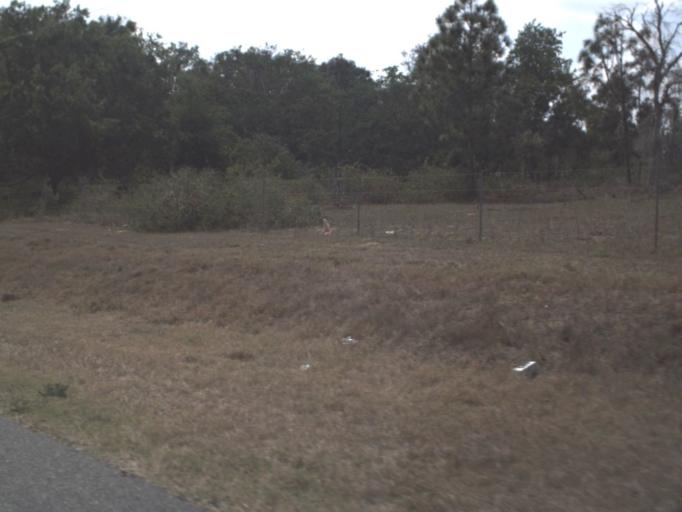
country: US
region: Florida
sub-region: Lake County
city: Groveland
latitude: 28.6032
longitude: -81.8384
